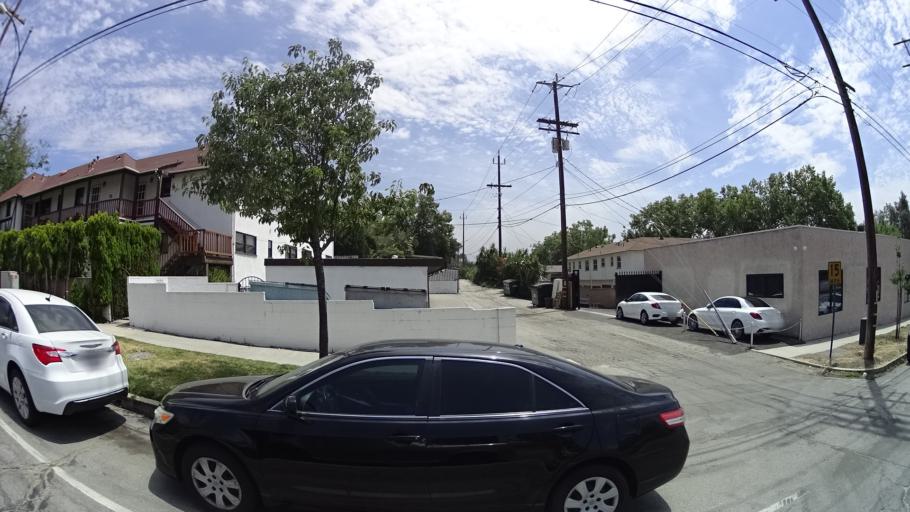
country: US
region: California
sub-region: Los Angeles County
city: Burbank
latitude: 34.1616
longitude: -118.3107
